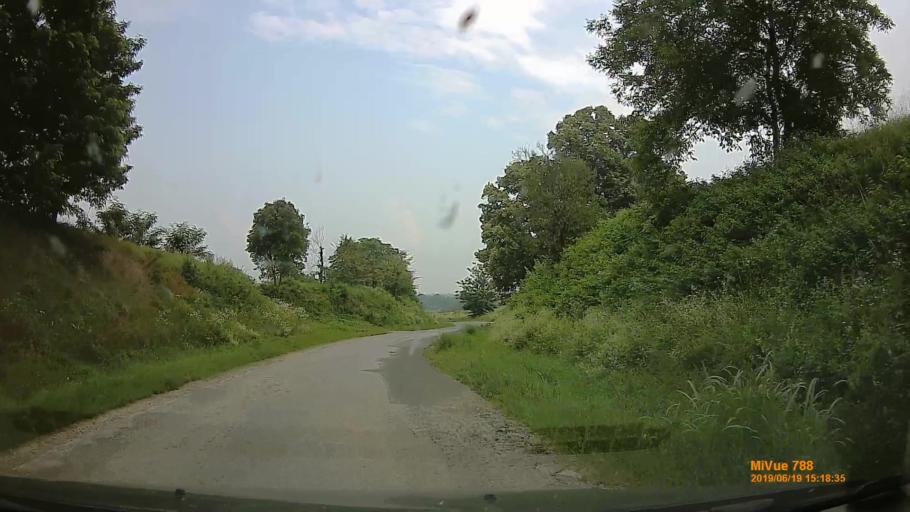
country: HU
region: Baranya
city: Szigetvar
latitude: 46.0760
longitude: 17.8572
